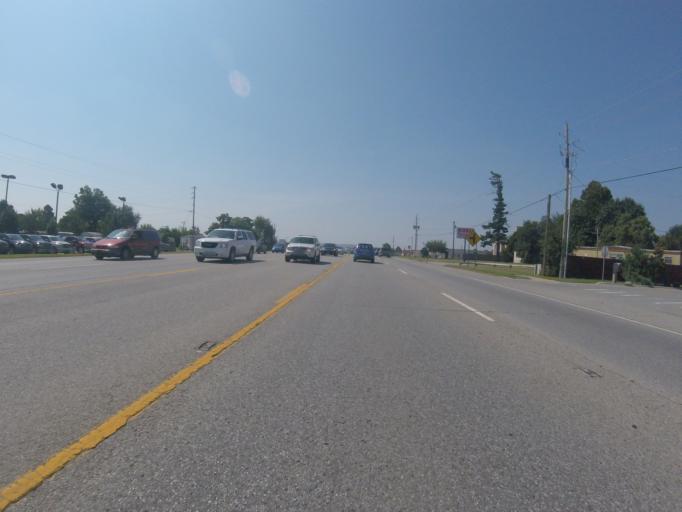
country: US
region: Arkansas
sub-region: Washington County
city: Johnson
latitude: 36.1515
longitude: -94.1440
